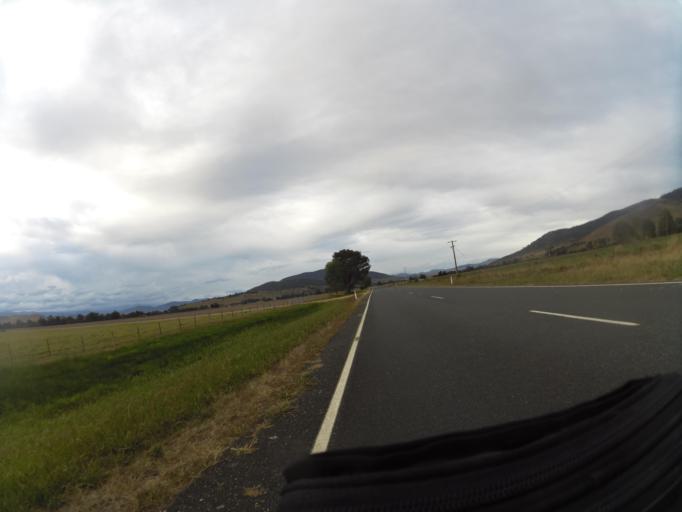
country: AU
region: New South Wales
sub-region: Snowy River
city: Jindabyne
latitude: -36.1015
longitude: 147.9810
